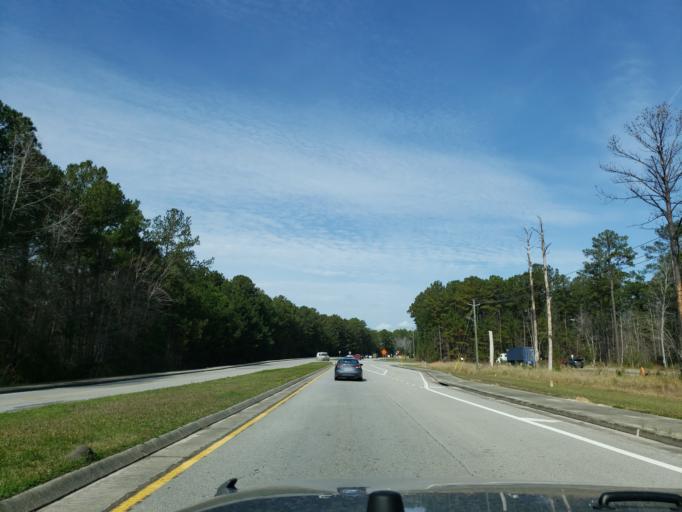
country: US
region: Georgia
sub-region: Chatham County
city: Pooler
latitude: 32.1653
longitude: -81.2335
